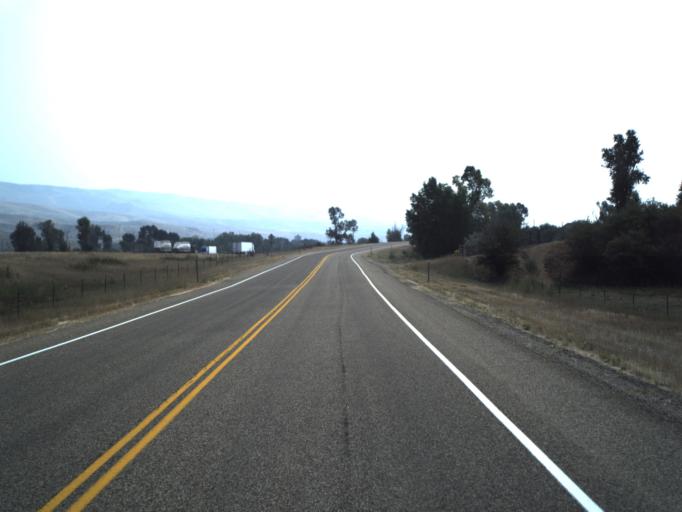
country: US
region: Utah
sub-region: Morgan County
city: Morgan
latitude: 41.0427
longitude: -111.5225
